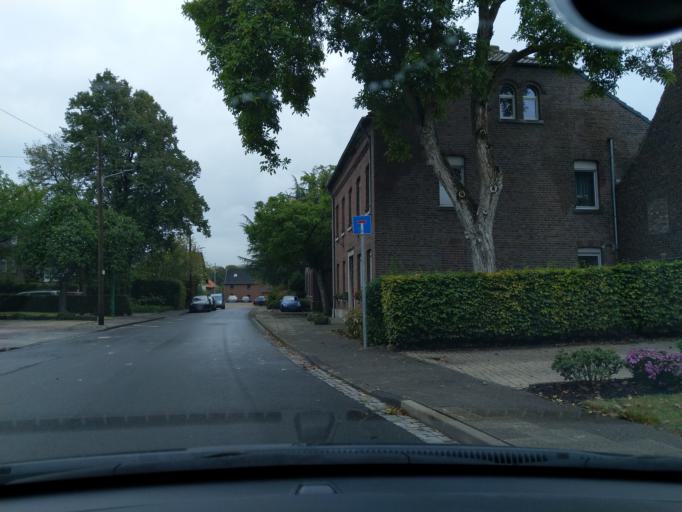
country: DE
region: North Rhine-Westphalia
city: Erkelenz
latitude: 51.0535
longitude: 6.3141
